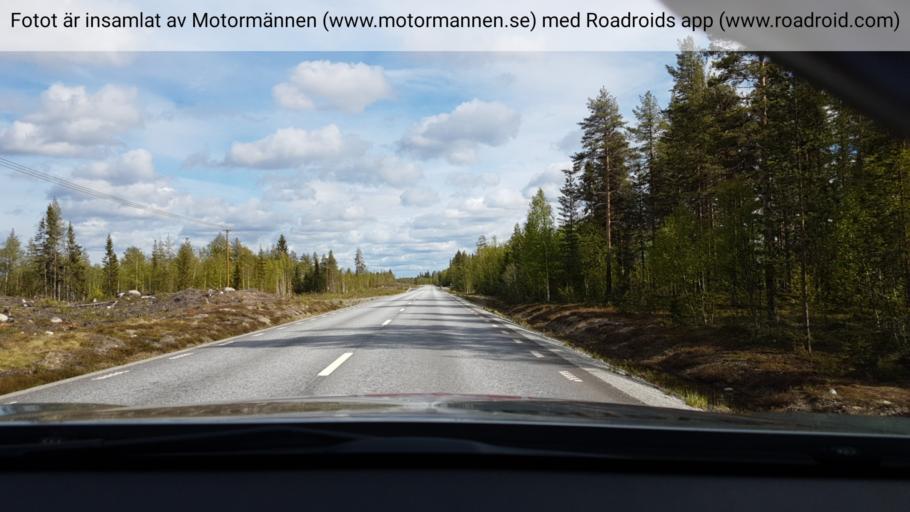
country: SE
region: Vaesternorrland
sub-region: OErnskoeldsviks Kommun
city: Bredbyn
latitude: 64.1130
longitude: 18.1158
